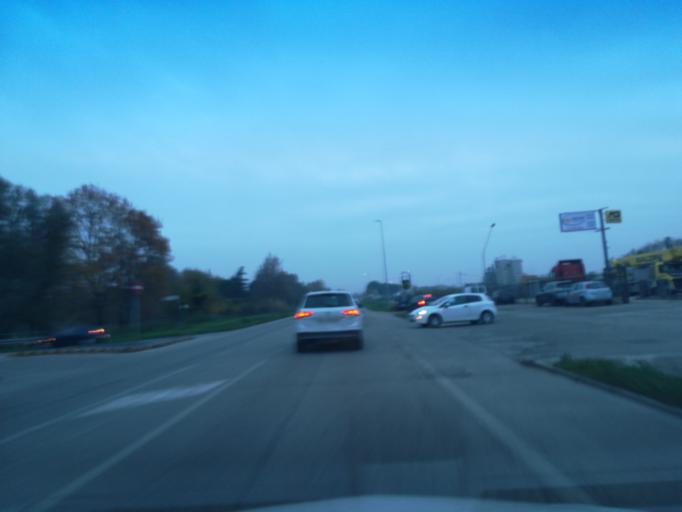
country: IT
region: Emilia-Romagna
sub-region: Provincia di Ravenna
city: Faenza
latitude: 44.3063
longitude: 11.8949
